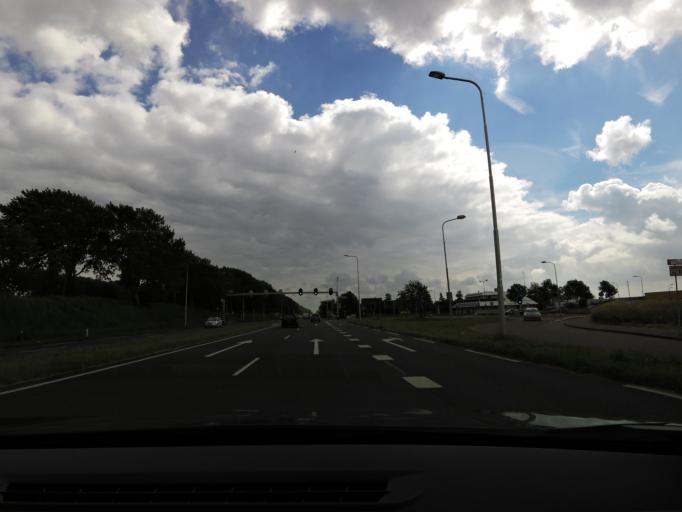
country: NL
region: Zeeland
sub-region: Gemeente Middelburg
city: Middelburg
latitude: 51.4755
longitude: 3.5988
